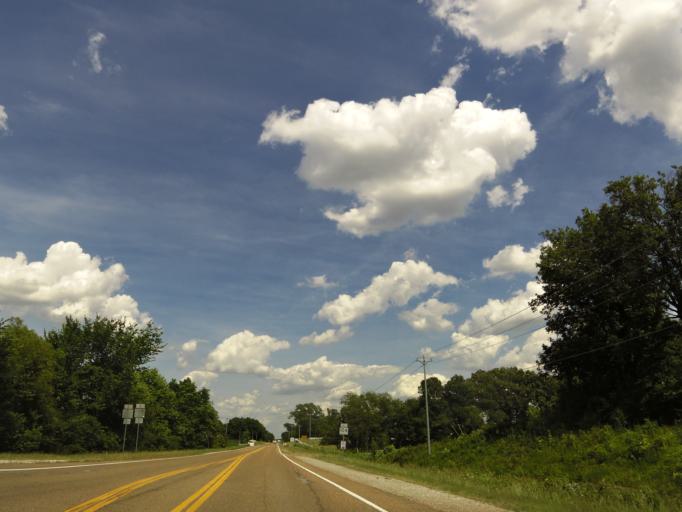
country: US
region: Tennessee
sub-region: Gibson County
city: Trenton
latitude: 35.9814
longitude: -88.9709
